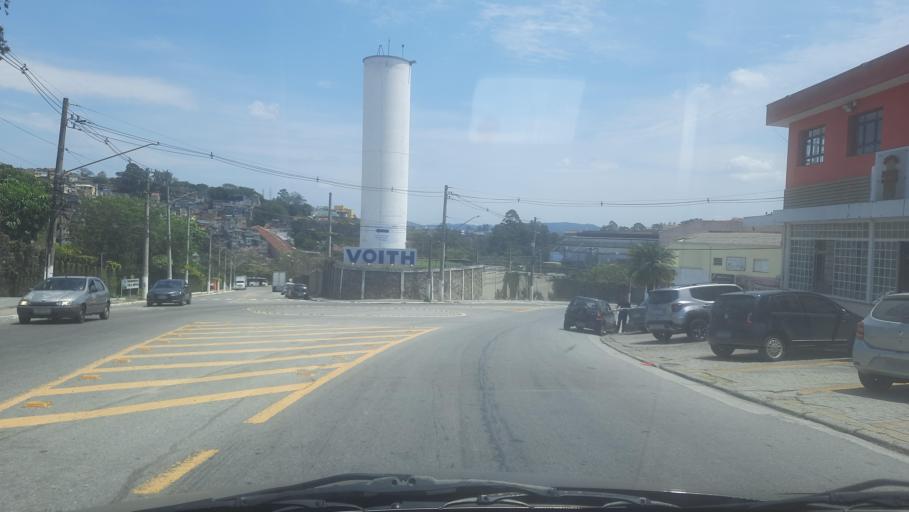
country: BR
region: Sao Paulo
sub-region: Caieiras
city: Caieiras
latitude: -23.4464
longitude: -46.7397
